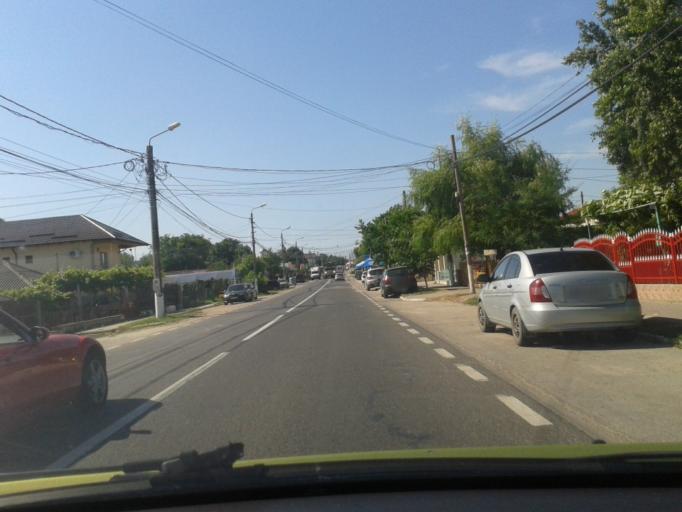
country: RO
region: Constanta
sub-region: Municipiul Mangalia
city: Mangalia
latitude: 43.7875
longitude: 28.5776
